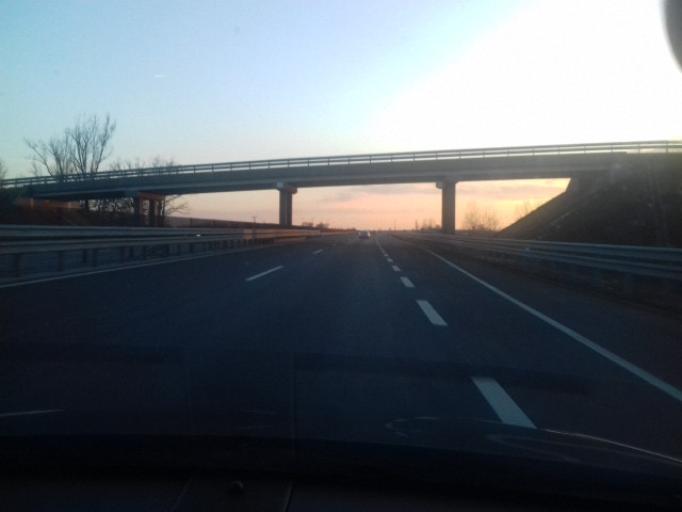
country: HU
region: Hajdu-Bihar
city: Gorbehaza
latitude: 47.8286
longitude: 21.3285
